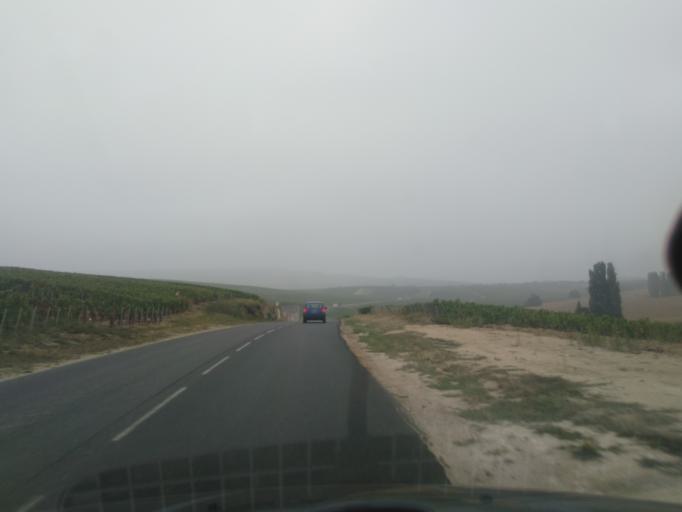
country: FR
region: Champagne-Ardenne
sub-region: Departement de la Marne
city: Mardeuil
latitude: 49.0736
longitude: 3.9432
